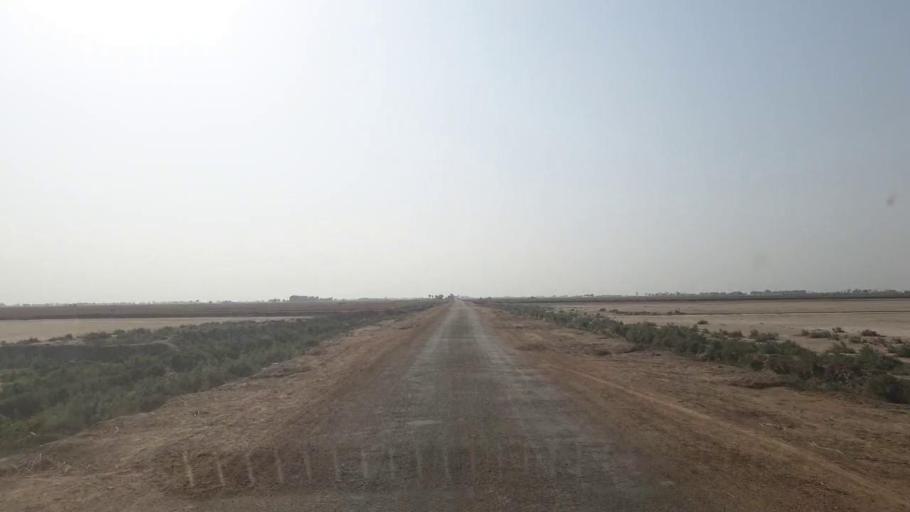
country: PK
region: Sindh
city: Kario
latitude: 24.5766
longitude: 68.5336
